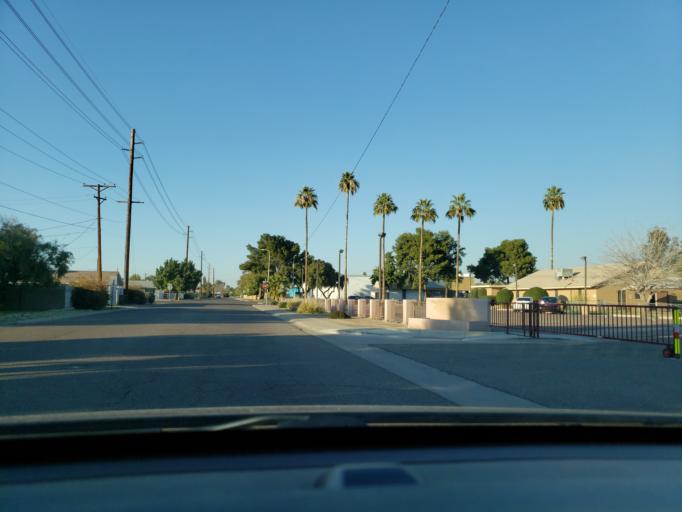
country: US
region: Arizona
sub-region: Maricopa County
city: Glendale
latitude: 33.5376
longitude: -112.1386
